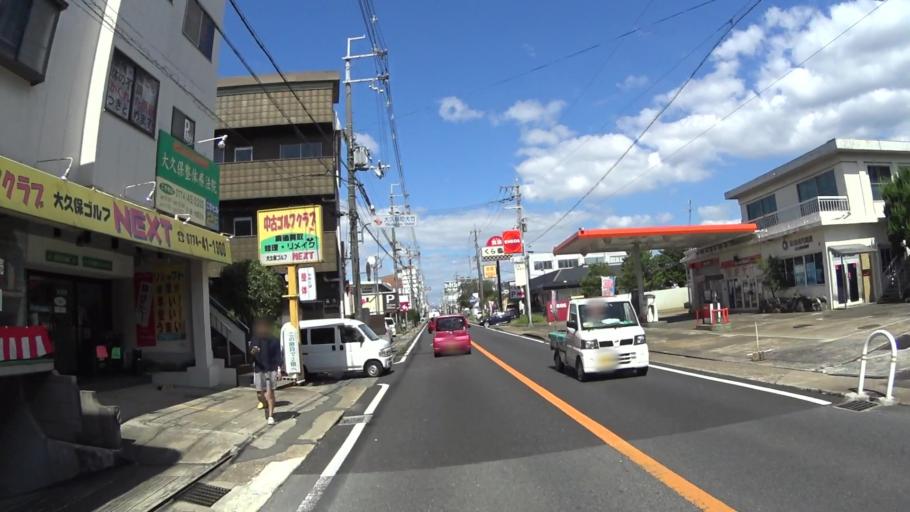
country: JP
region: Kyoto
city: Uji
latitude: 34.8688
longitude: 135.7774
